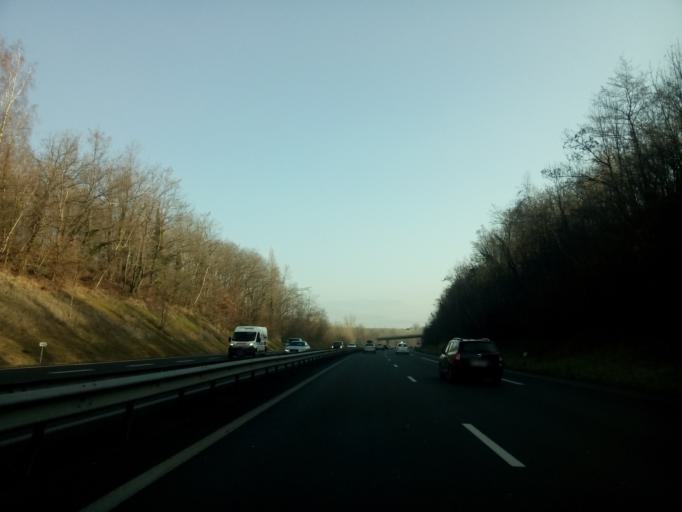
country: FR
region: Rhone-Alpes
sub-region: Departement de l'Isere
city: Fitilieu
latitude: 45.5700
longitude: 5.5544
